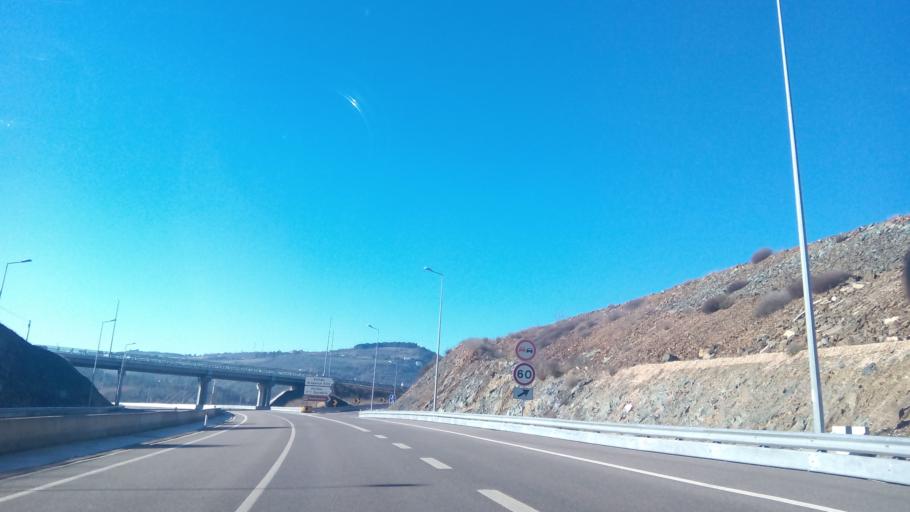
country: PT
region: Braganca
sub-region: Braganca Municipality
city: Braganca
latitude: 41.7918
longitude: -6.7191
